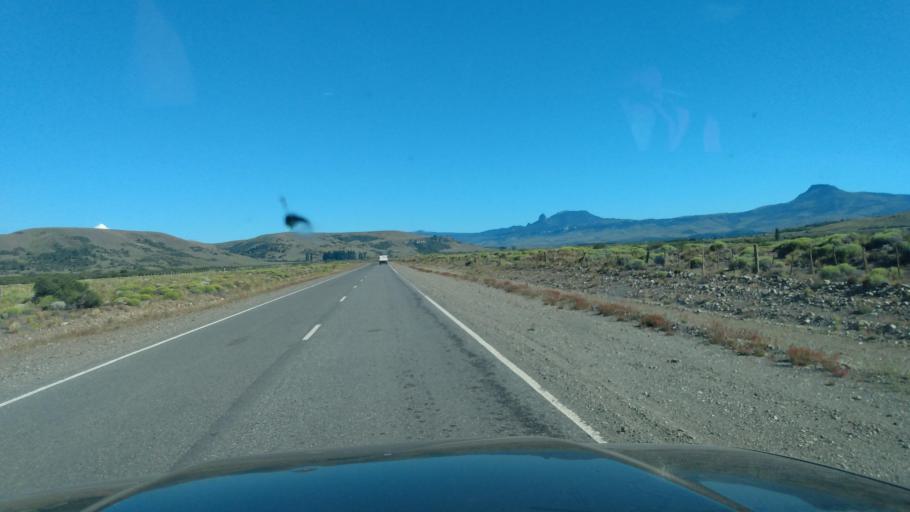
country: AR
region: Neuquen
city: Junin de los Andes
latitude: -39.8698
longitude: -71.1765
